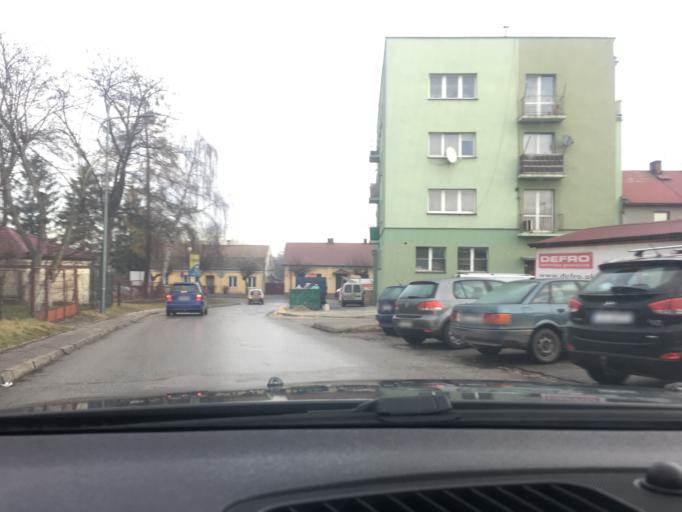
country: PL
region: Swietokrzyskie
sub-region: Powiat jedrzejowski
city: Jedrzejow
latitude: 50.6454
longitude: 20.2937
